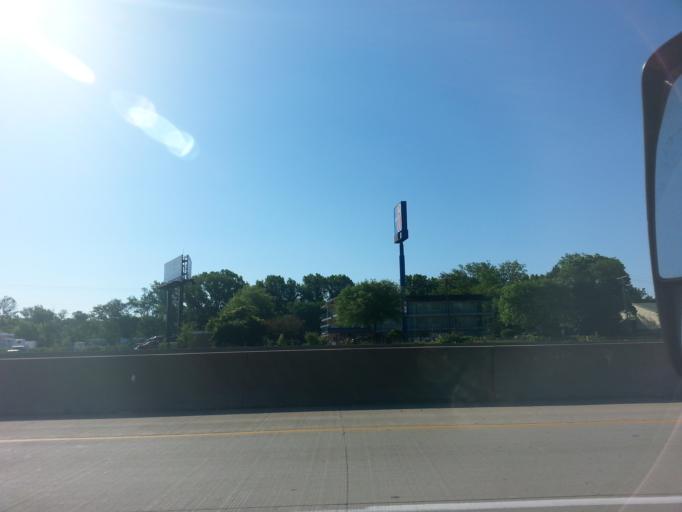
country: US
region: Indiana
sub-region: Clark County
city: Clarksville
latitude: 38.2970
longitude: -85.7553
